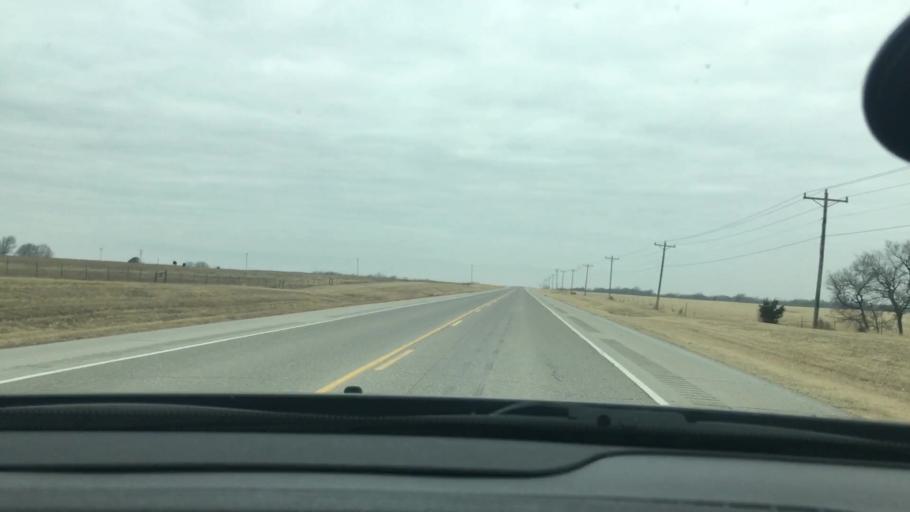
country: US
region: Oklahoma
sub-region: Murray County
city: Davis
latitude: 34.5213
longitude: -97.2917
